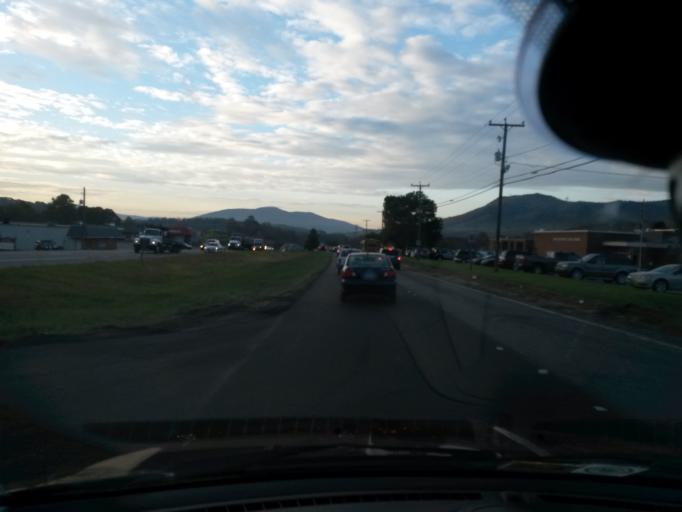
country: US
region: Virginia
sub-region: Botetourt County
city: Daleville
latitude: 37.4065
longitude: -79.9139
